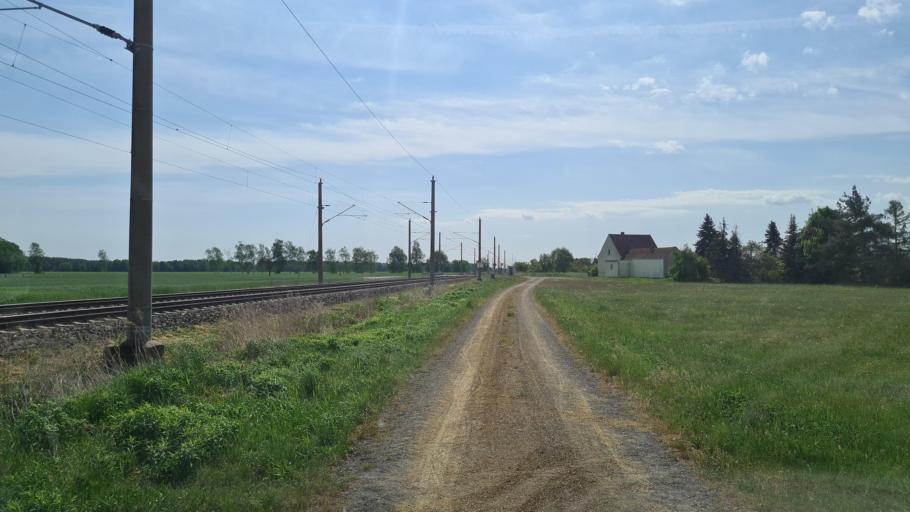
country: DE
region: Brandenburg
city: Falkenberg
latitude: 51.5573
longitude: 13.2923
